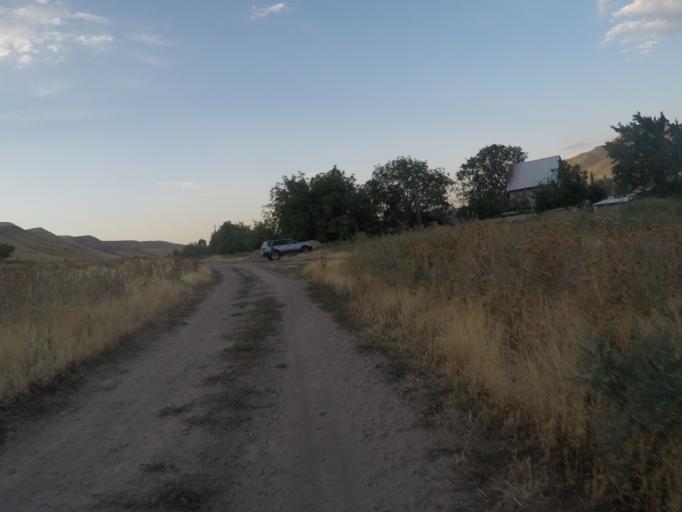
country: KG
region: Chuy
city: Bishkek
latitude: 42.7665
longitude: 74.6384
